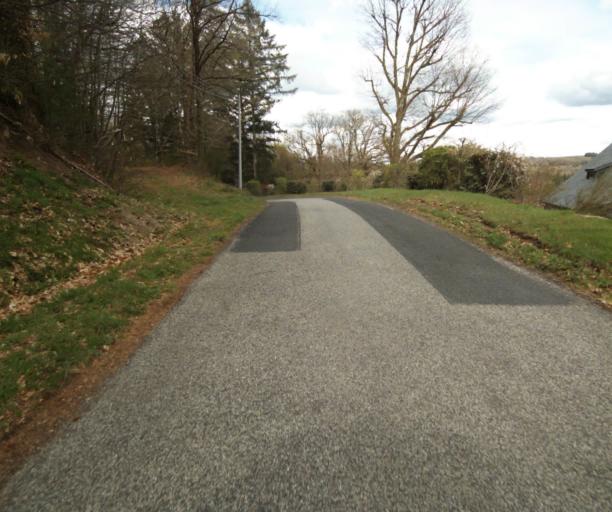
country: FR
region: Limousin
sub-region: Departement de la Correze
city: Argentat
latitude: 45.2008
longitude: 1.9634
